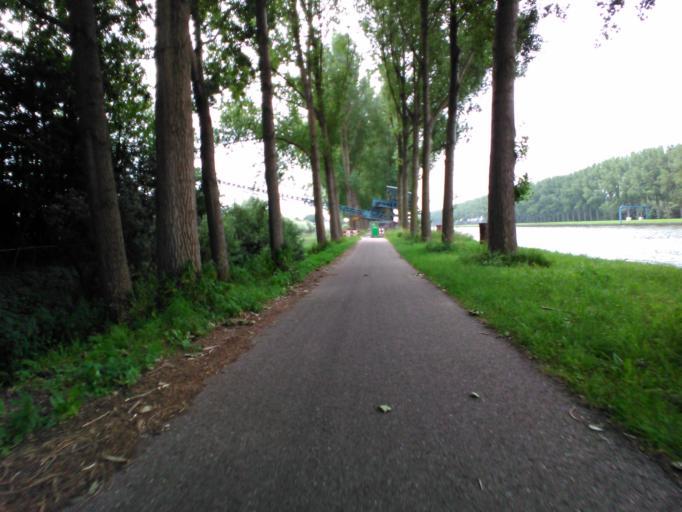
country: NL
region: North Holland
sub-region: Gemeente Amsterdam
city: Driemond
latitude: 52.3209
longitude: 5.0189
